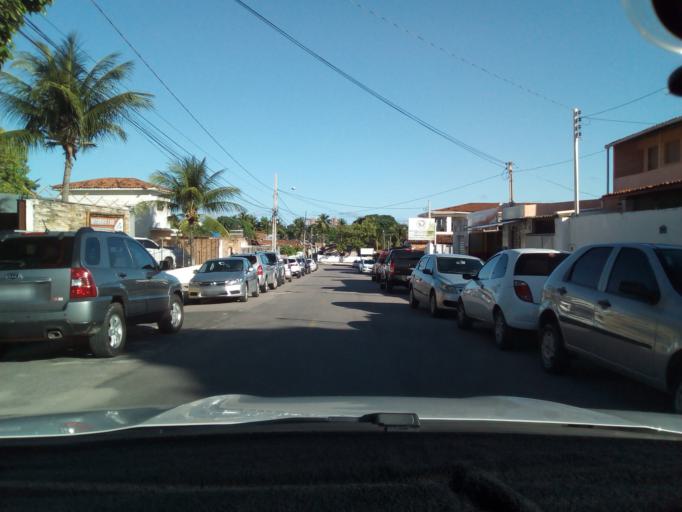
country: BR
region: Paraiba
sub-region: Joao Pessoa
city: Joao Pessoa
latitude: -7.1382
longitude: -34.8304
